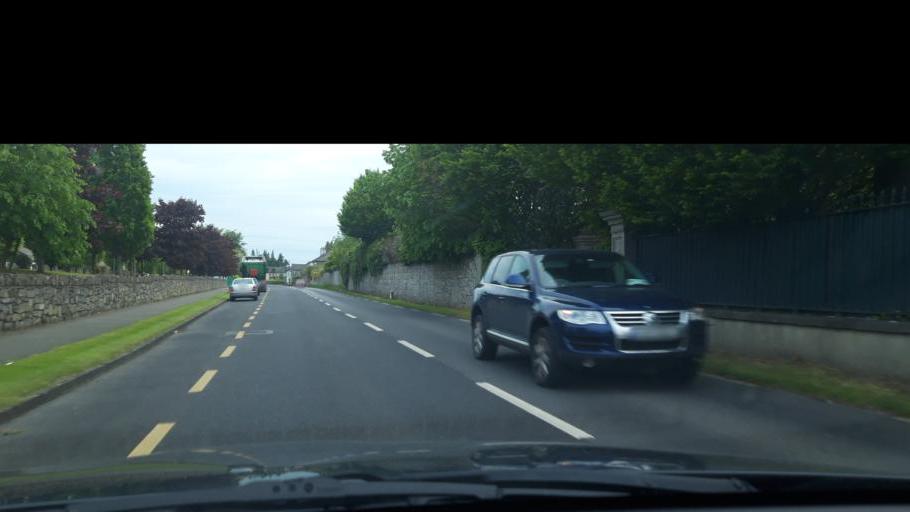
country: IE
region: Leinster
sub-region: Kildare
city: Celbridge
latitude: 53.3304
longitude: -6.5485
